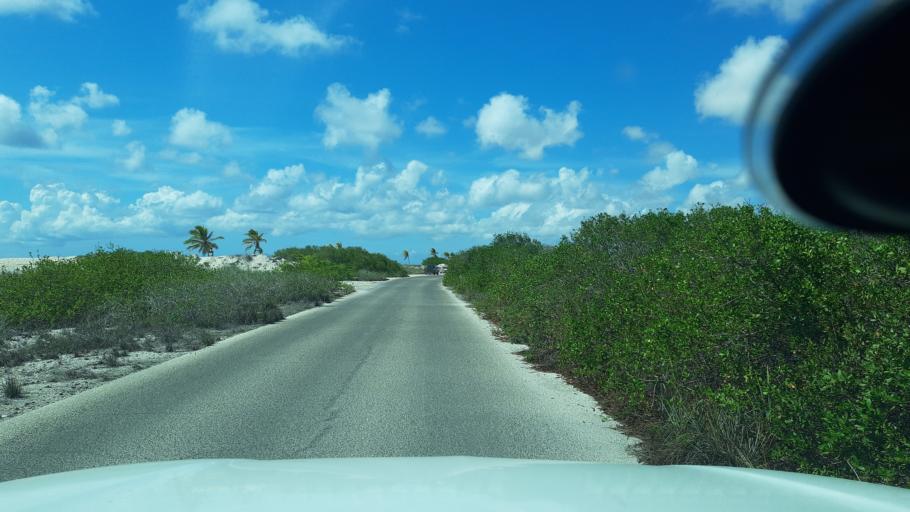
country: BQ
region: Bonaire
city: Dorp Tera Kora
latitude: 12.0598
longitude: -68.2813
